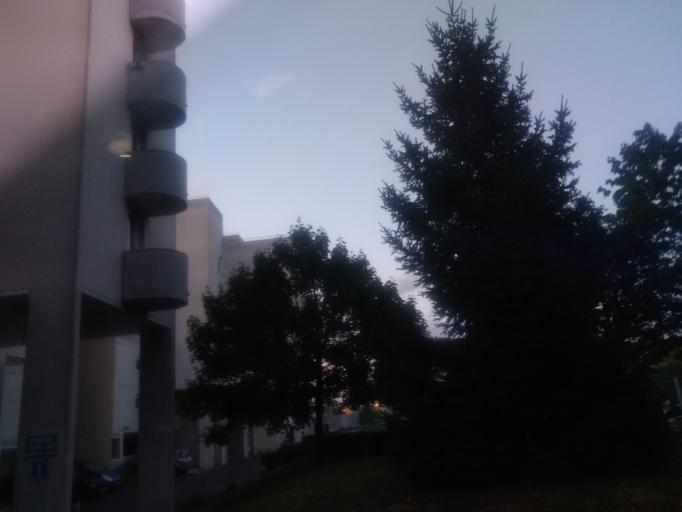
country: FR
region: Ile-de-France
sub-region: Departement de Seine-et-Marne
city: Noisiel
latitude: 48.8413
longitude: 2.6168
